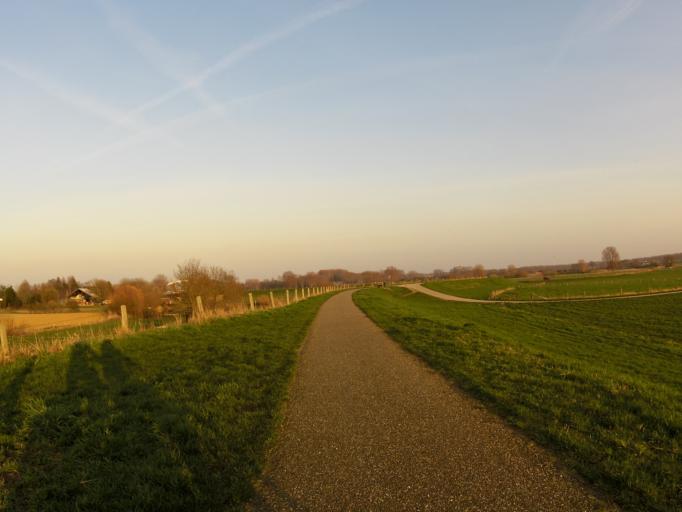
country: NL
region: Gelderland
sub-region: Gemeente Maasdriel
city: Hedel
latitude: 51.7399
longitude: 5.2528
